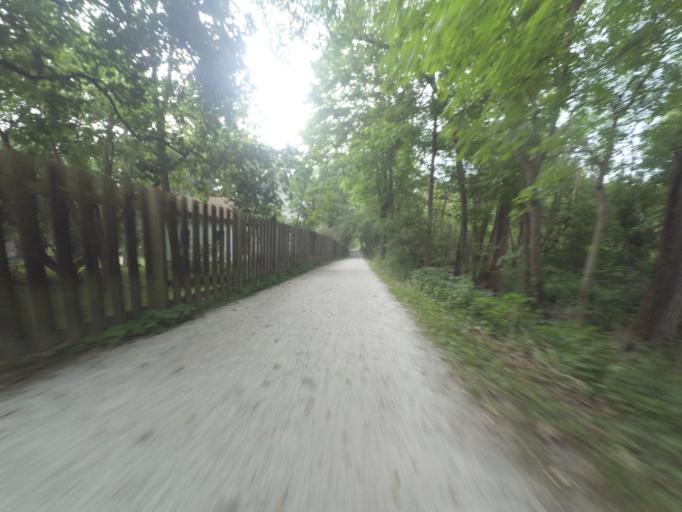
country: US
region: Ohio
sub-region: Summit County
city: Peninsula
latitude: 41.2643
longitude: -81.5587
